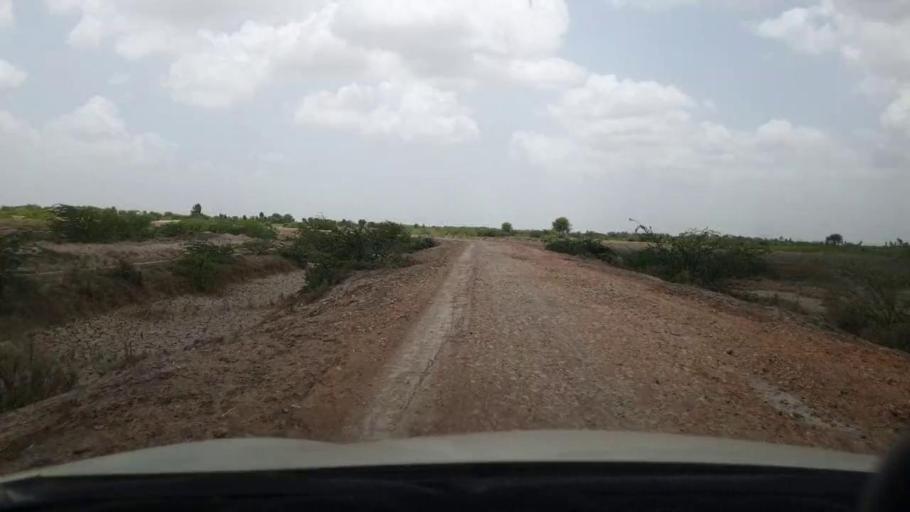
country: PK
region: Sindh
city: Kadhan
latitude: 24.3804
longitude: 68.9301
